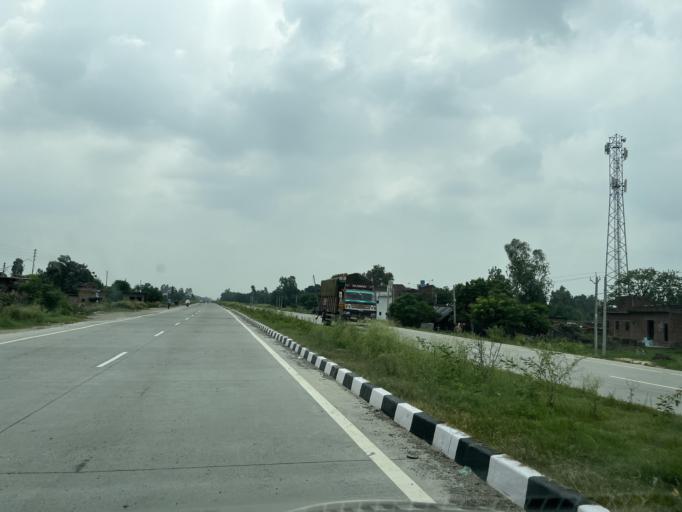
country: IN
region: Uttar Pradesh
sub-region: Bijnor
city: Najibabad
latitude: 29.5499
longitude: 78.3394
